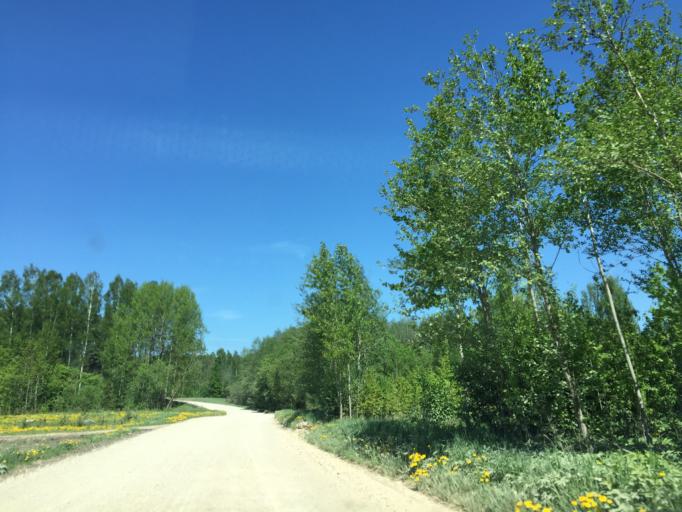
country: LV
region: Ikskile
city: Ikskile
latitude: 56.8699
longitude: 24.5022
